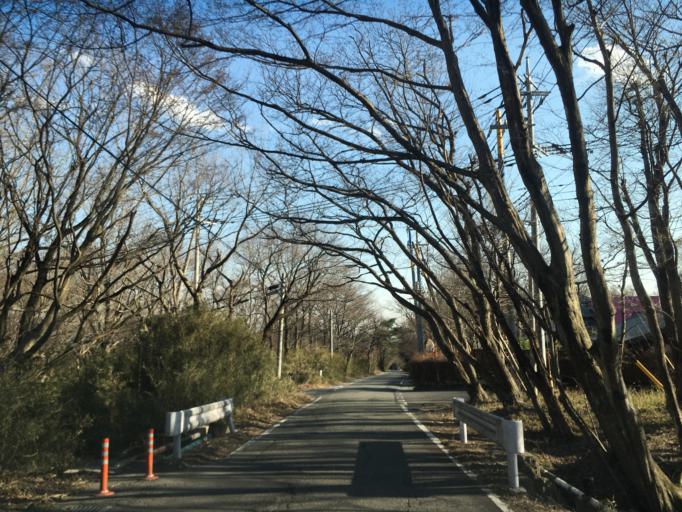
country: JP
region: Tochigi
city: Kuroiso
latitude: 37.0659
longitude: 140.0043
